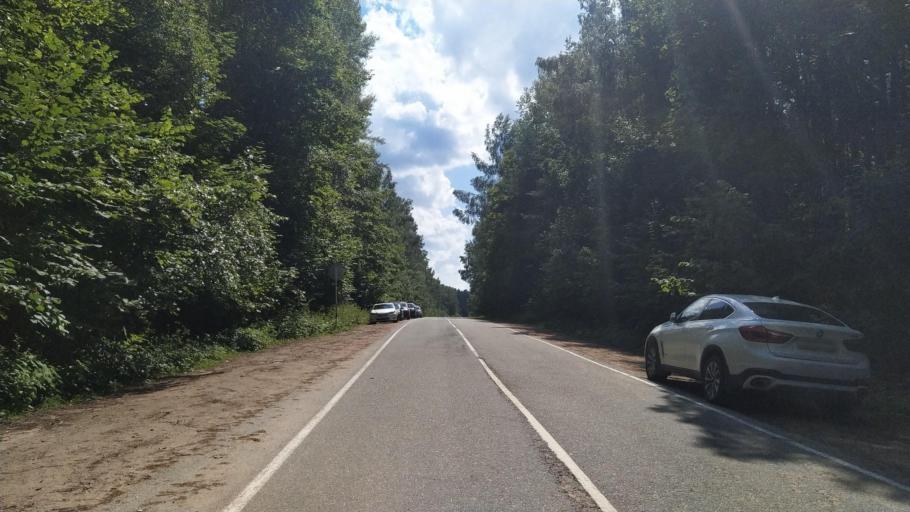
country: RU
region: Pskov
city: Pushkinskiye Gory
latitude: 57.0746
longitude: 28.9564
